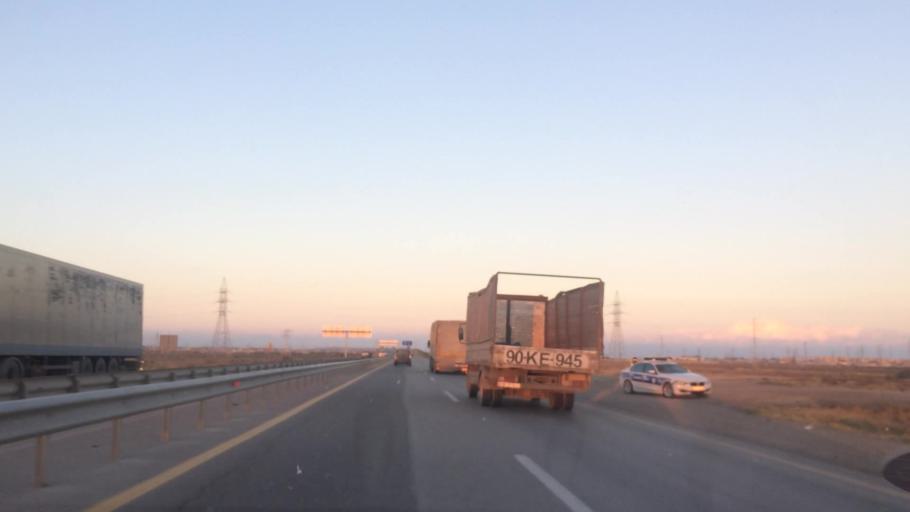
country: AZ
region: Baki
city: Qobustan
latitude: 39.9555
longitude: 49.3817
